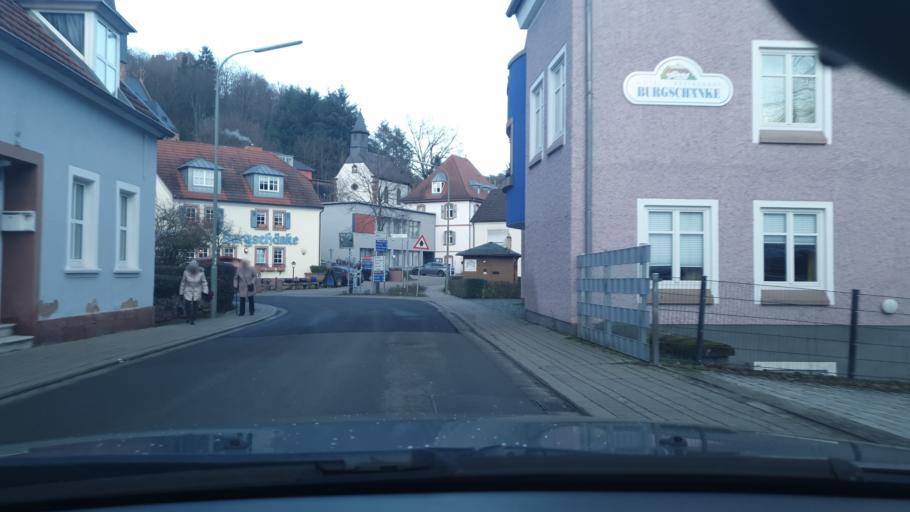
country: DE
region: Rheinland-Pfalz
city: Stelzenberg
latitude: 49.4120
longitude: 7.6984
